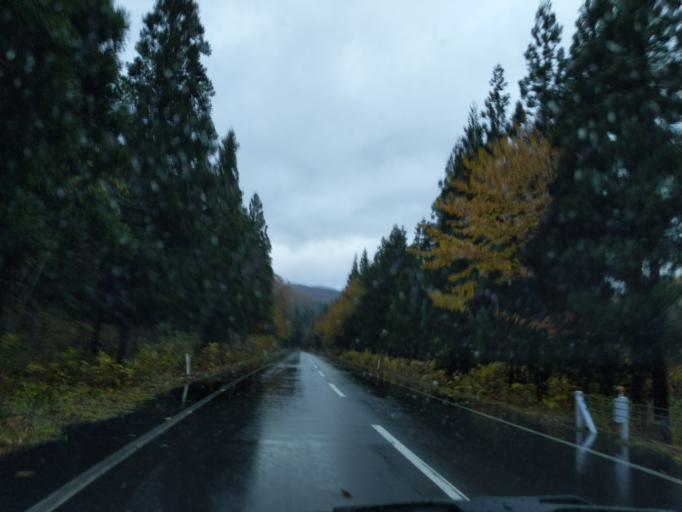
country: JP
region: Iwate
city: Mizusawa
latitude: 39.0815
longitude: 140.8615
